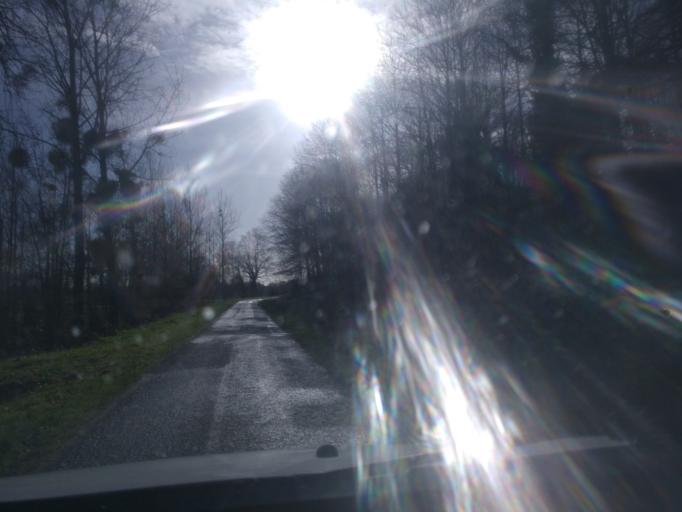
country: FR
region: Brittany
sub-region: Departement d'Ille-et-Vilaine
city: Antrain
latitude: 48.4999
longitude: -1.5001
